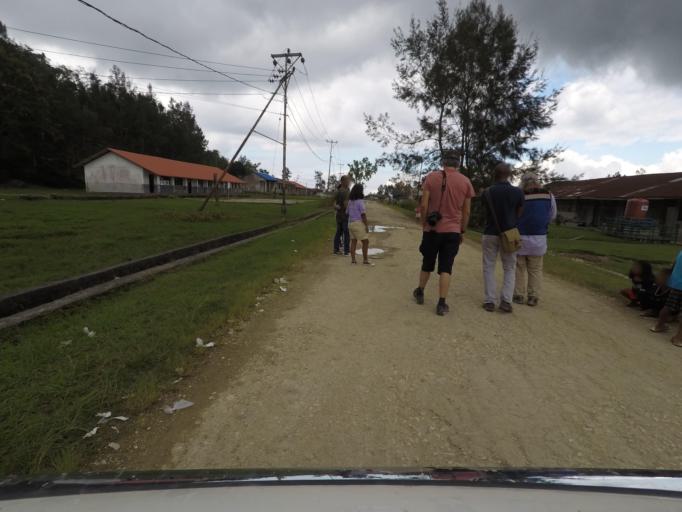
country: TL
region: Baucau
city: Venilale
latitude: -8.7356
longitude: 126.3694
